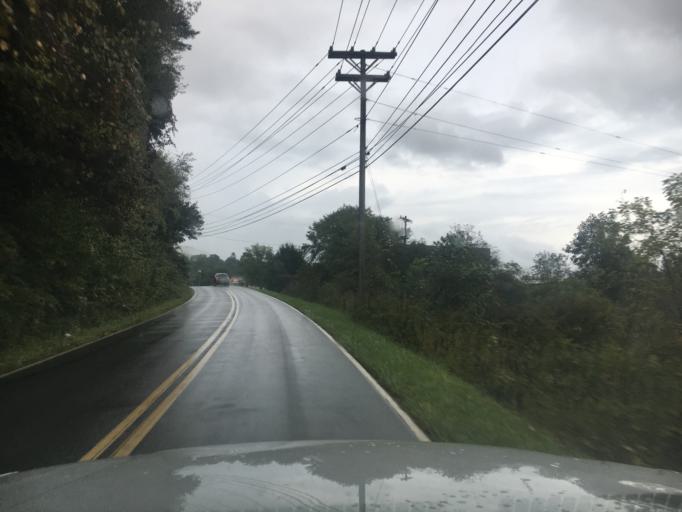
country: US
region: North Carolina
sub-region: Transylvania County
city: Brevard
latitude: 35.2589
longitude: -82.6795
